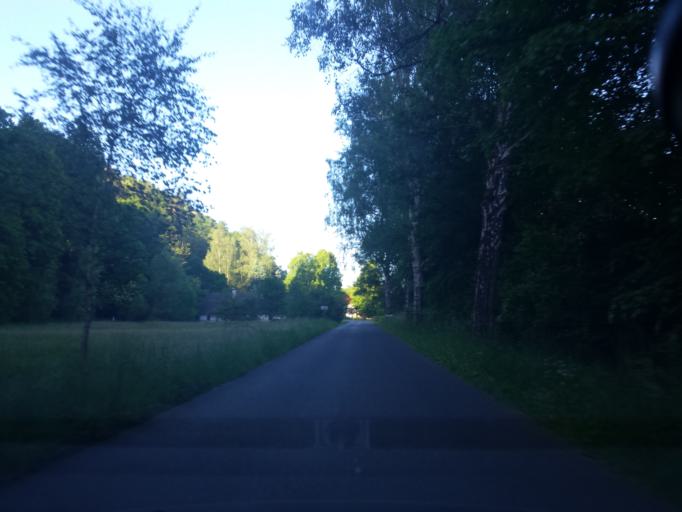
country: CZ
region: Central Bohemia
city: Mseno
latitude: 50.4610
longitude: 14.5953
